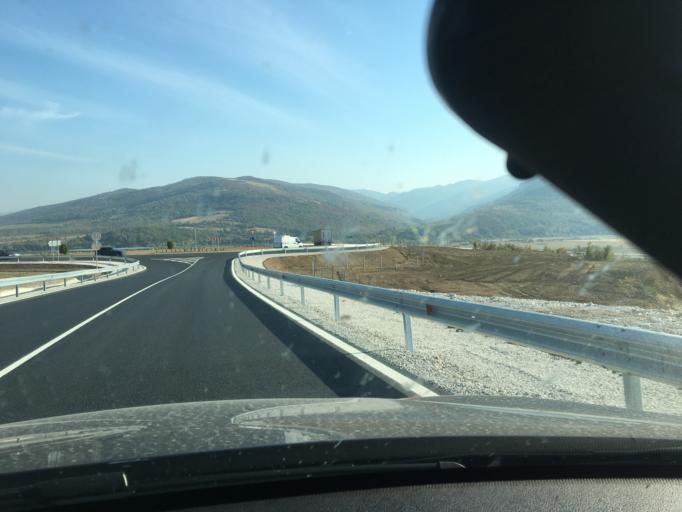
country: BG
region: Lovech
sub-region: Obshtina Yablanitsa
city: Yablanitsa
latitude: 43.0574
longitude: 24.2215
